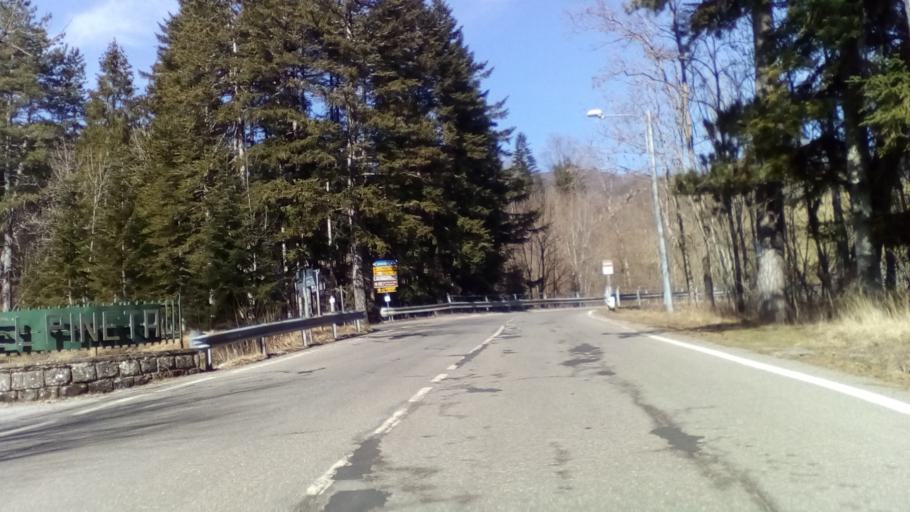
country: IT
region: Emilia-Romagna
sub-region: Provincia di Modena
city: Pievepelago
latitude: 44.2092
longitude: 10.6093
